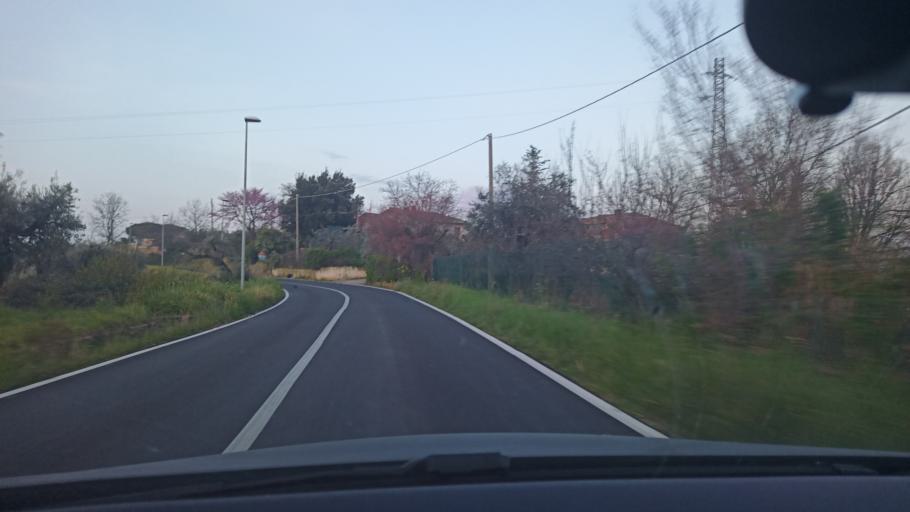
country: IT
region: Latium
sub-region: Provincia di Rieti
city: Torri in Sabina
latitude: 42.3405
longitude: 12.6509
